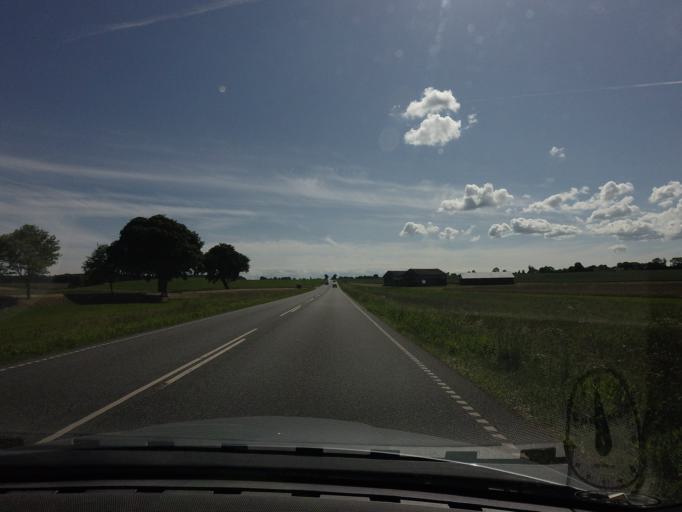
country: DK
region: Central Jutland
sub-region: Syddjurs Kommune
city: Ebeltoft
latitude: 56.3248
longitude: 10.7138
